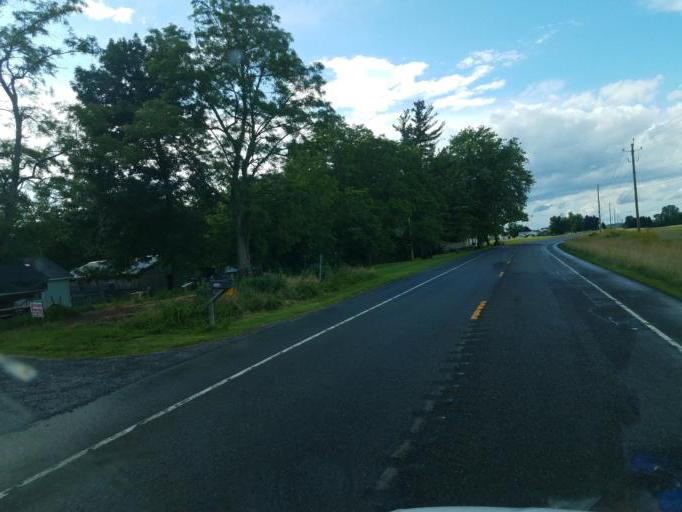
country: US
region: New York
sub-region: Wayne County
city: Clyde
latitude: 43.0089
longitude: -76.8568
